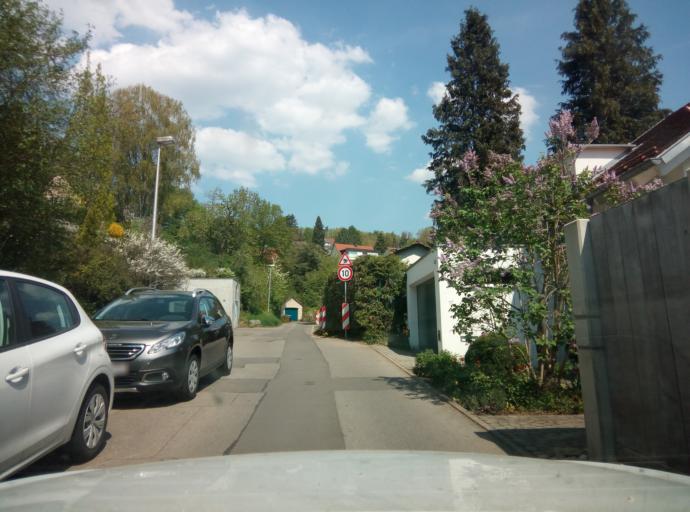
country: DE
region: Baden-Wuerttemberg
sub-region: Tuebingen Region
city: Tuebingen
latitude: 48.5311
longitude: 9.0551
